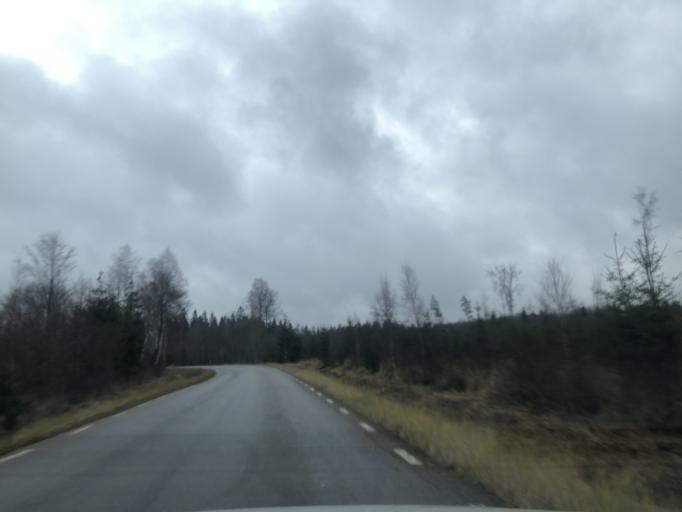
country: SE
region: Vaestra Goetaland
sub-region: Ulricehamns Kommun
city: Ulricehamn
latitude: 57.8947
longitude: 13.5030
